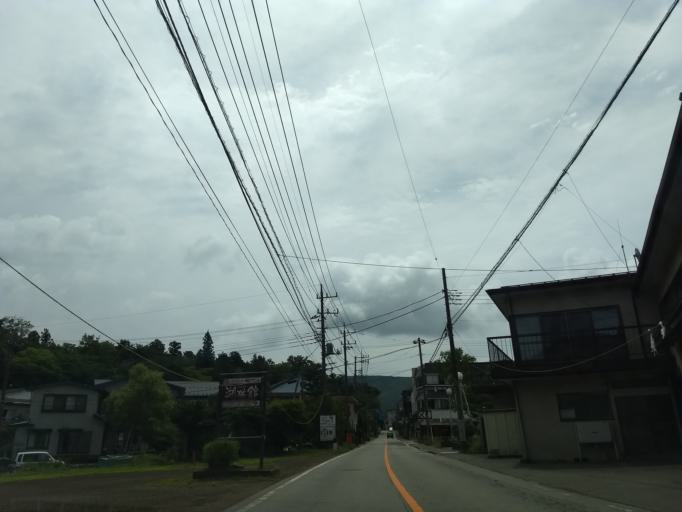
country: JP
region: Shizuoka
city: Gotemba
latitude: 35.4282
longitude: 138.9001
